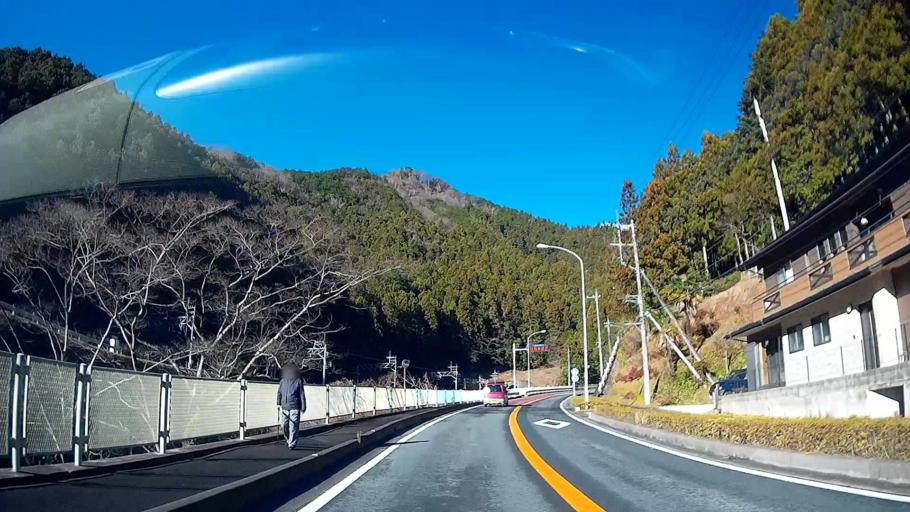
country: JP
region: Saitama
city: Chichibu
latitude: 35.9392
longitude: 139.1811
